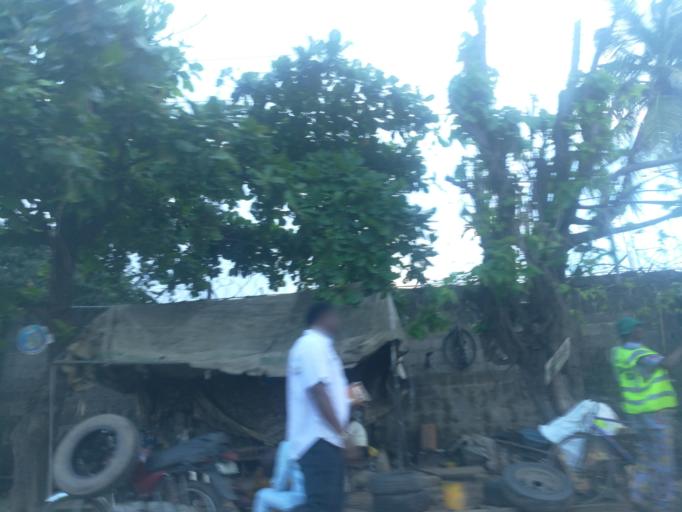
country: NG
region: Lagos
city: Somolu
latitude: 6.5505
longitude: 3.3776
